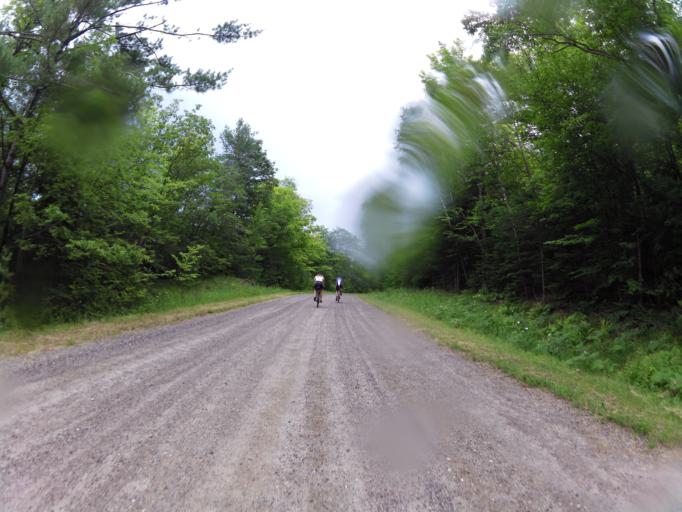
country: CA
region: Ontario
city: Renfrew
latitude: 45.1059
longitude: -76.6109
